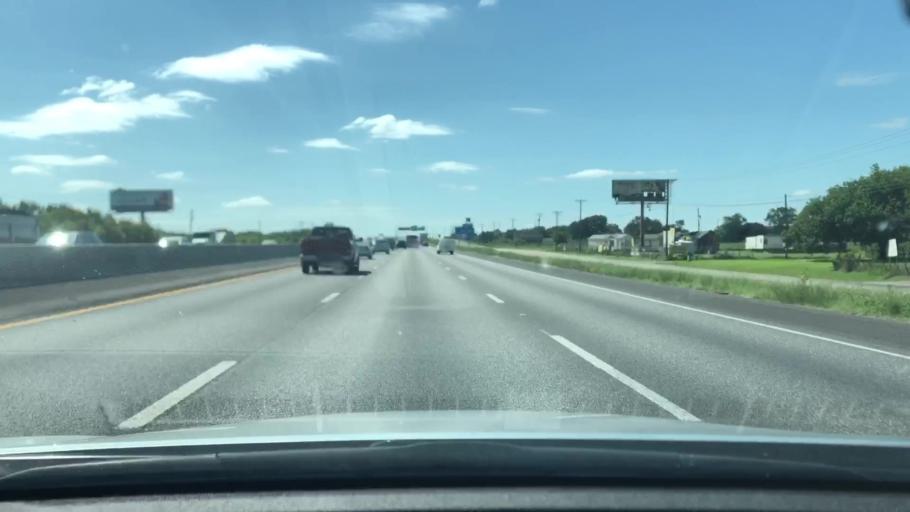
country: US
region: Texas
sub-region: Guadalupe County
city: Lake Dunlap
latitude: 29.7552
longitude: -98.0523
